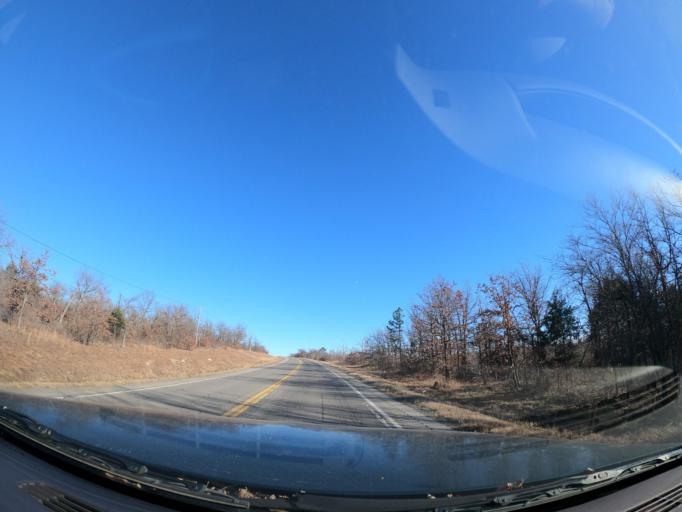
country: US
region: Oklahoma
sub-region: Pittsburg County
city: Longtown
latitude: 35.2256
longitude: -95.4446
